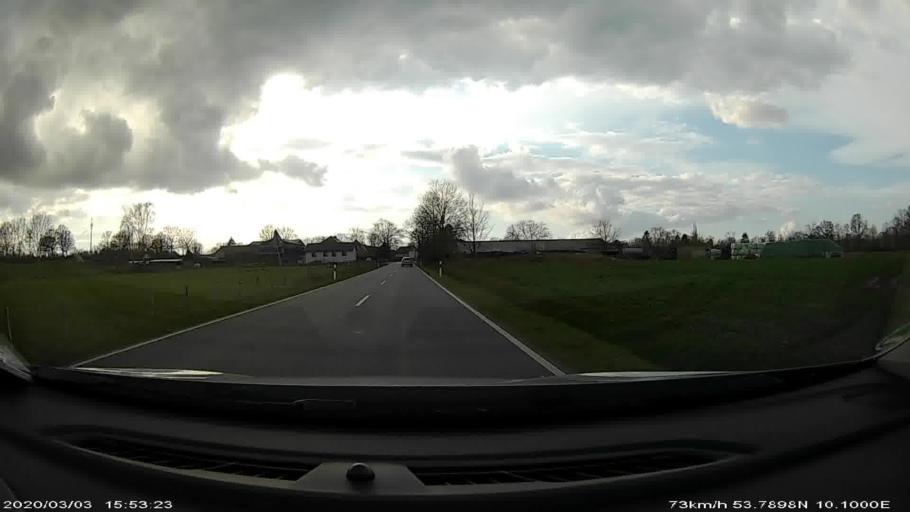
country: DE
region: Schleswig-Holstein
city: Nahe
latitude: 53.7903
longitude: 10.1020
